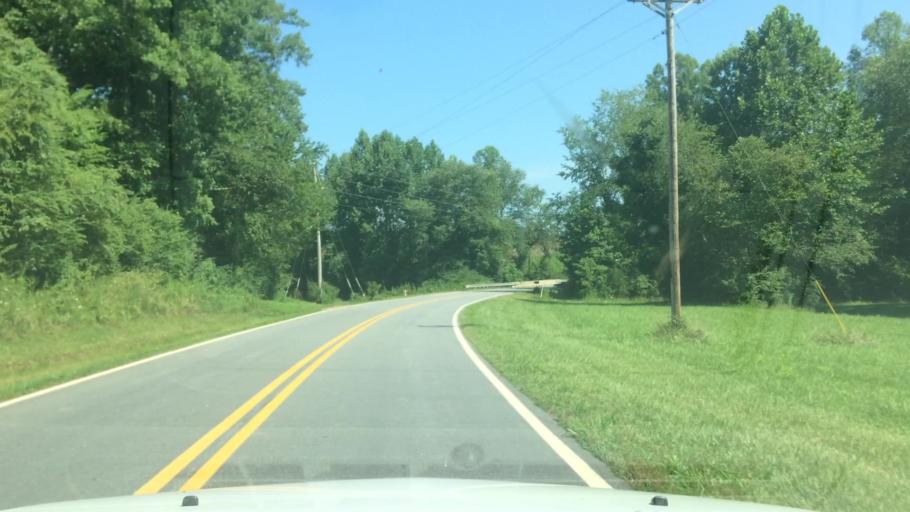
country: US
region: North Carolina
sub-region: Alexander County
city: Taylorsville
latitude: 35.9581
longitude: -81.2692
